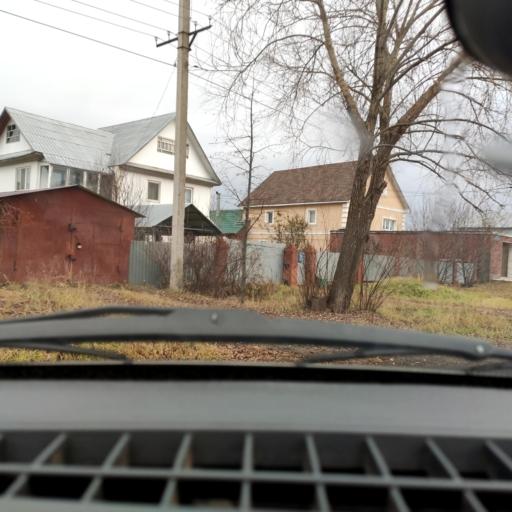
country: RU
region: Bashkortostan
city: Ufa
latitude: 54.6497
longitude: 55.9261
